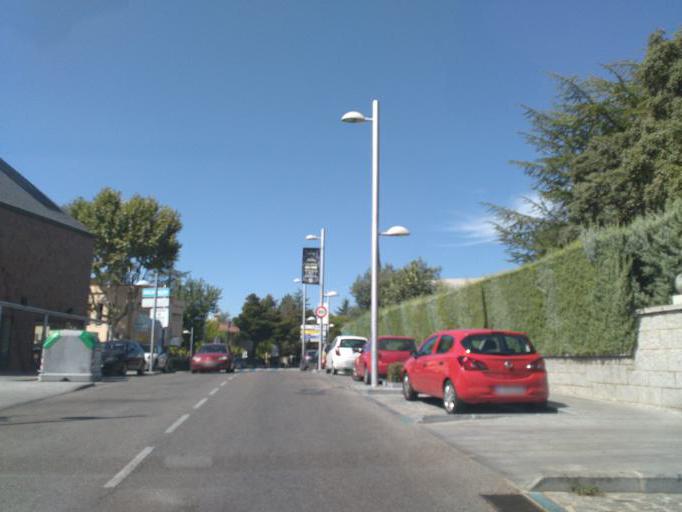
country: ES
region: Madrid
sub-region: Provincia de Madrid
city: Torrelodones
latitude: 40.5792
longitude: -3.9557
